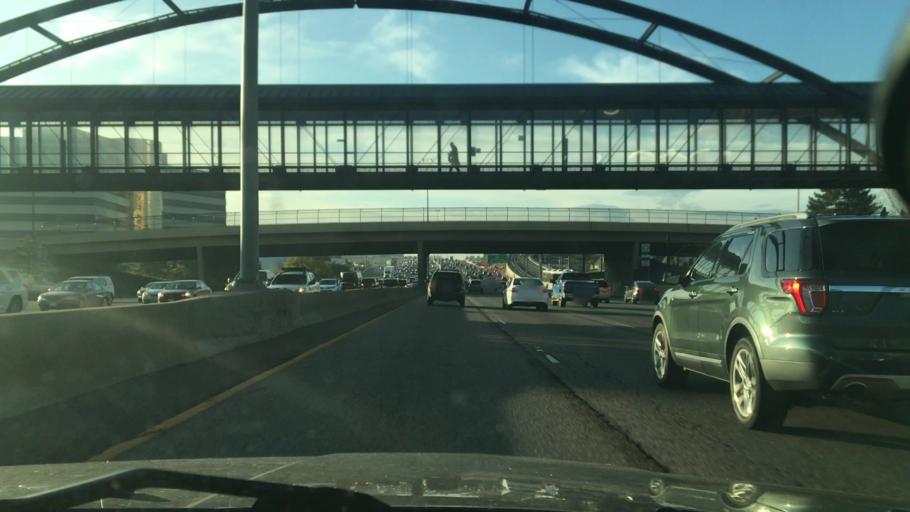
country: US
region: Colorado
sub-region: Arapahoe County
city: Castlewood
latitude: 39.6010
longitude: -104.8884
